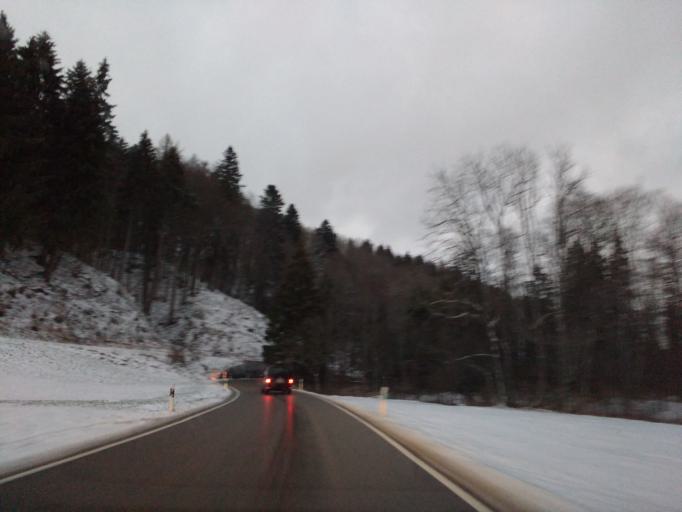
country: DE
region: Bavaria
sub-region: Swabia
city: Buchenberg
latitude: 47.7079
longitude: 10.2582
